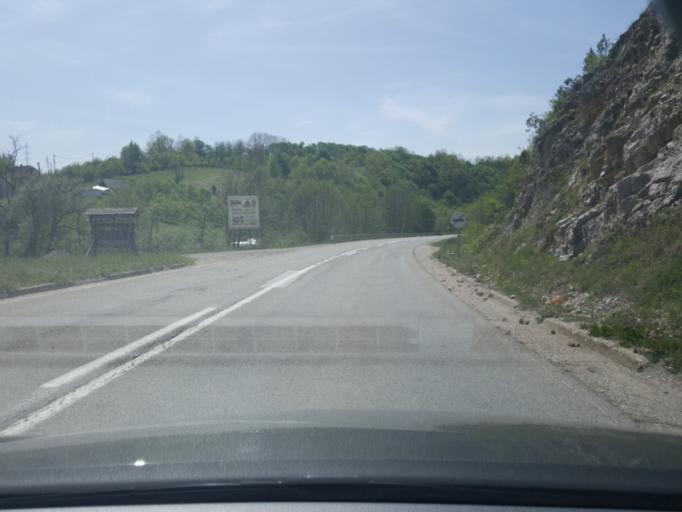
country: RS
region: Central Serbia
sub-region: Zlatiborski Okrug
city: Cajetina
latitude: 43.7876
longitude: 19.7250
